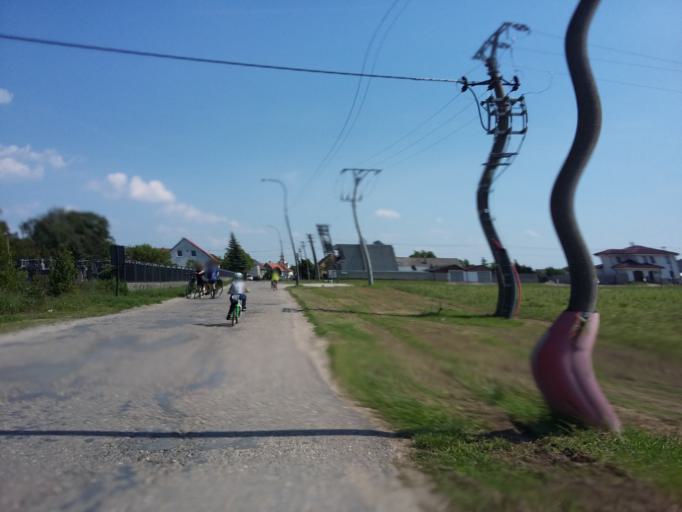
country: AT
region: Lower Austria
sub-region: Politischer Bezirk Ganserndorf
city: Drosing
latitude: 48.5064
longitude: 16.9667
